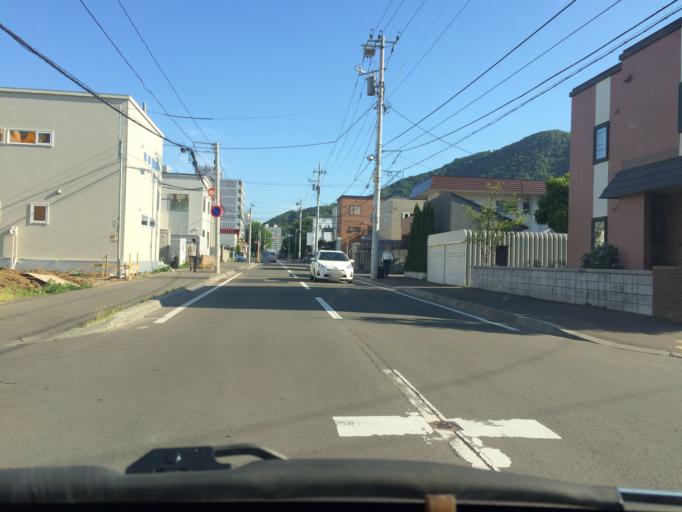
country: JP
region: Hokkaido
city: Sapporo
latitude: 43.0319
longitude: 141.3412
